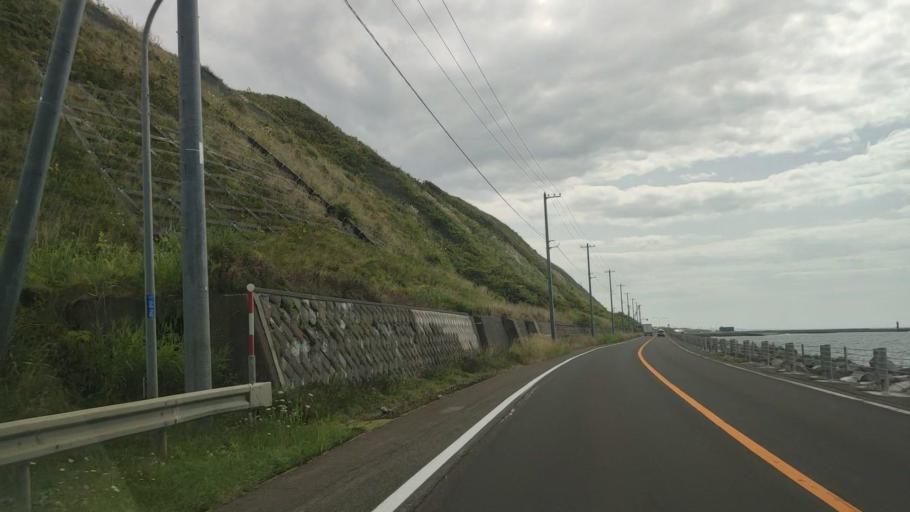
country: JP
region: Hokkaido
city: Rumoi
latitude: 44.5432
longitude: 141.7666
